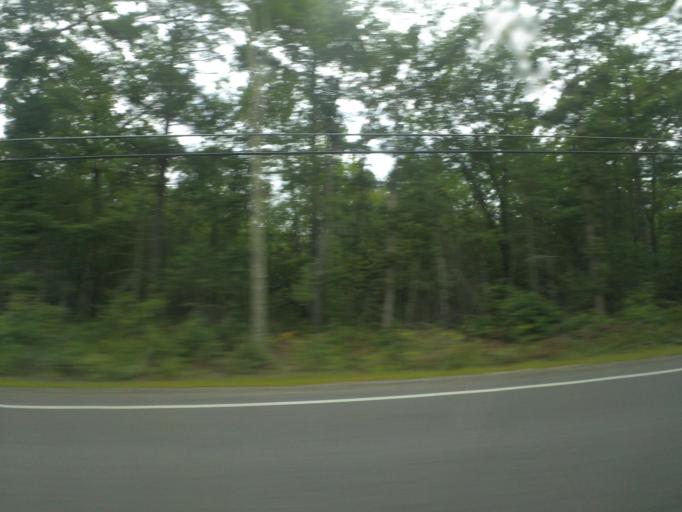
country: US
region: New Hampshire
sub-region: Strafford County
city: Barrington
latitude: 43.2571
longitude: -71.0293
